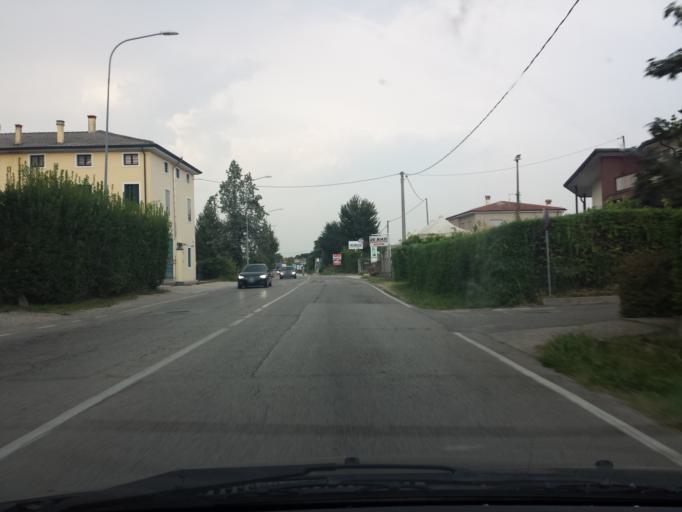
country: IT
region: Veneto
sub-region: Provincia di Vicenza
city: Monticello Conte Otto
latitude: 45.5832
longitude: 11.5543
